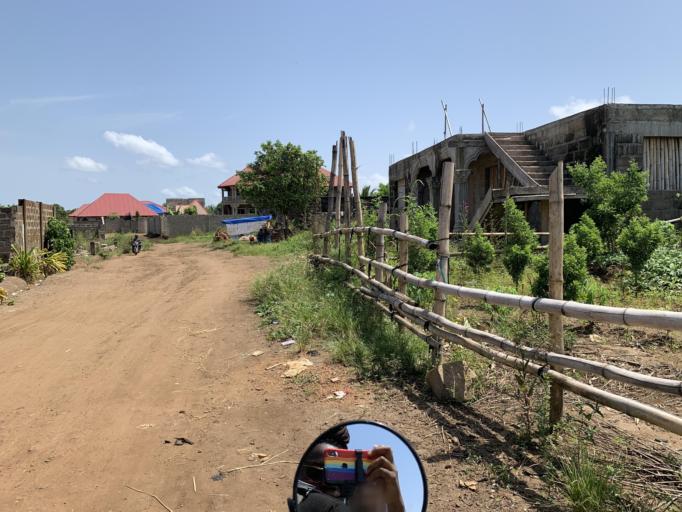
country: SL
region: Western Area
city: Hastings
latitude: 8.3941
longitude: -13.1337
